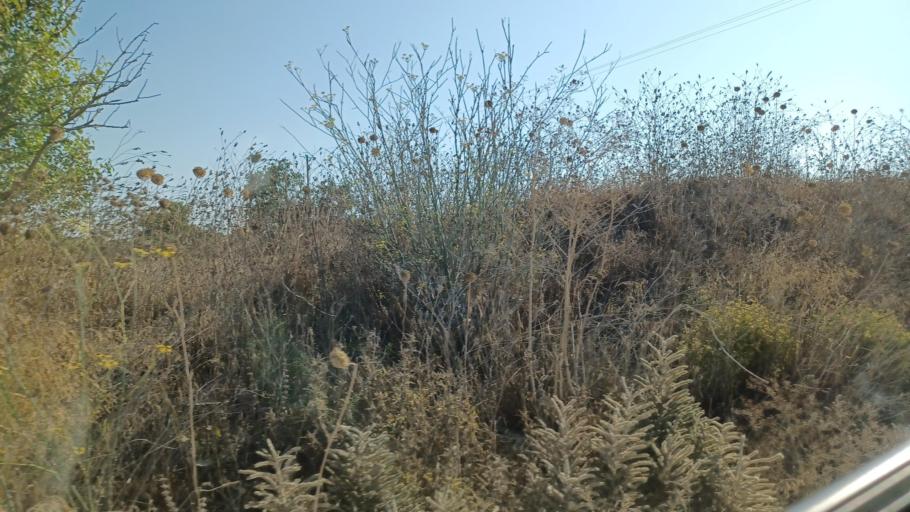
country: CY
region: Pafos
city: Mesogi
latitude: 34.8714
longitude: 32.5048
